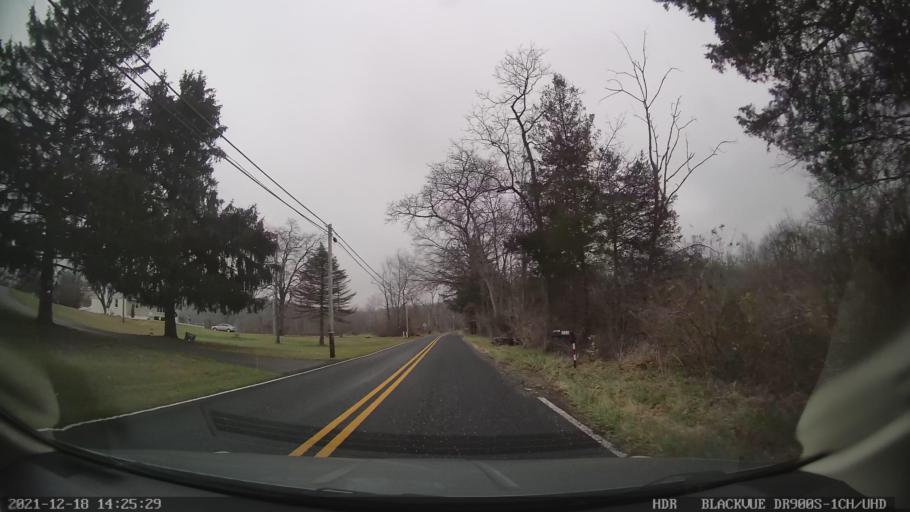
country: US
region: Pennsylvania
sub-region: Berks County
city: Oley
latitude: 40.4151
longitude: -75.7415
